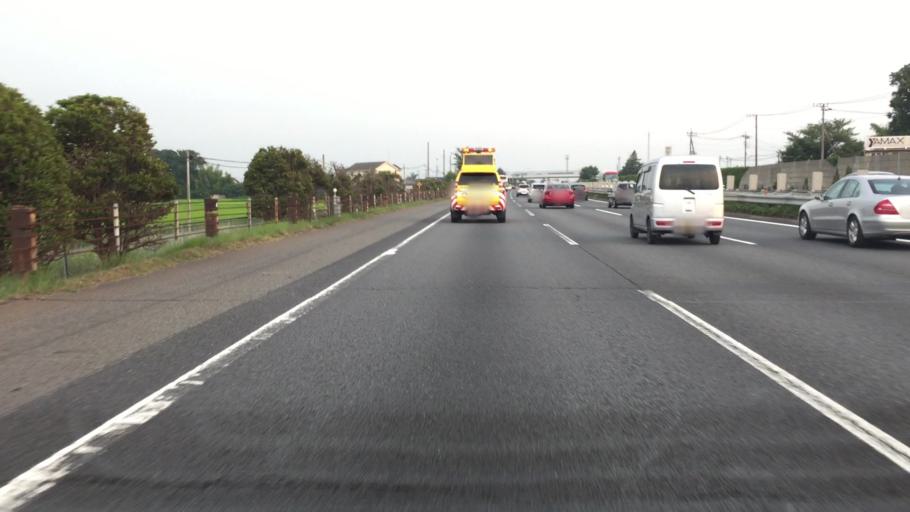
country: JP
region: Saitama
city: Hanyu
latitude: 36.1890
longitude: 139.5845
